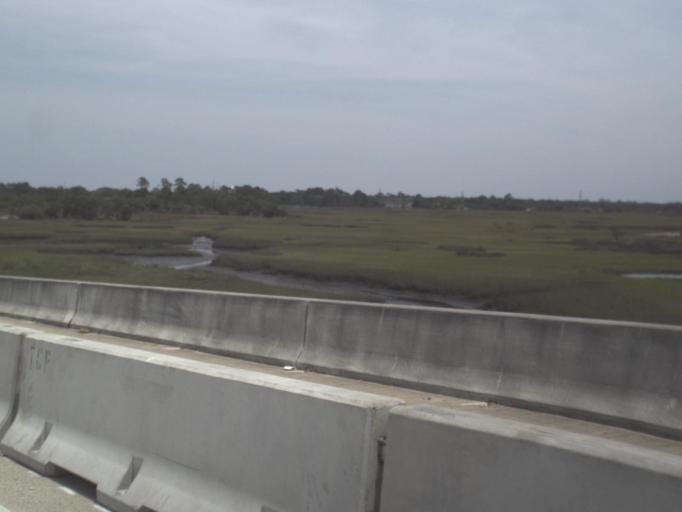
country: US
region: Florida
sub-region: Duval County
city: Atlantic Beach
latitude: 30.3240
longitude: -81.4353
